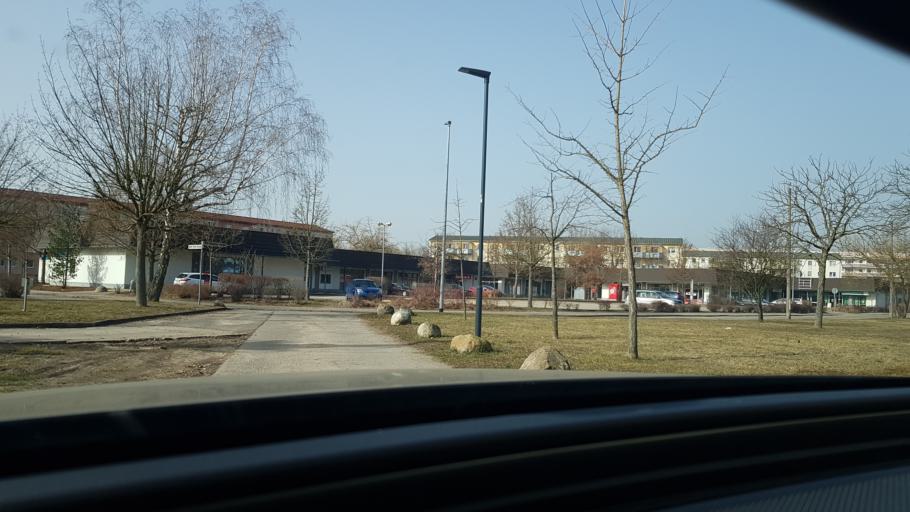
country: DE
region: Brandenburg
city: Guben
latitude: 51.9372
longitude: 14.6988
